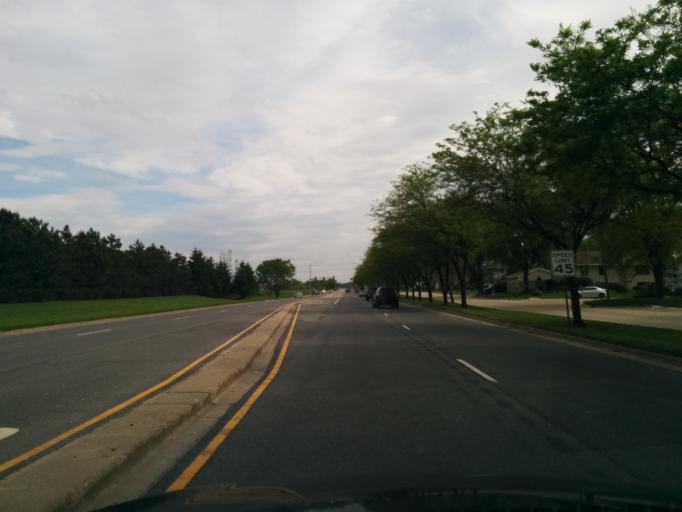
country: US
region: Illinois
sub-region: Will County
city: Romeoville
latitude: 41.6377
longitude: -88.0805
